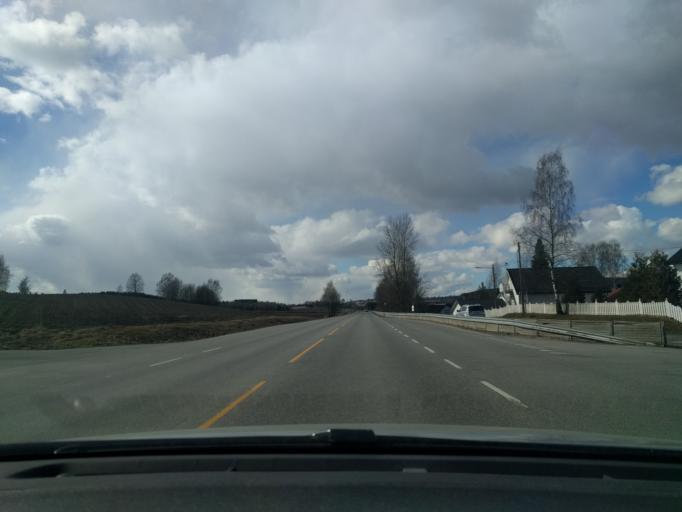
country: NO
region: Hedmark
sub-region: Hamar
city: Hamar
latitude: 60.8360
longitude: 11.0558
